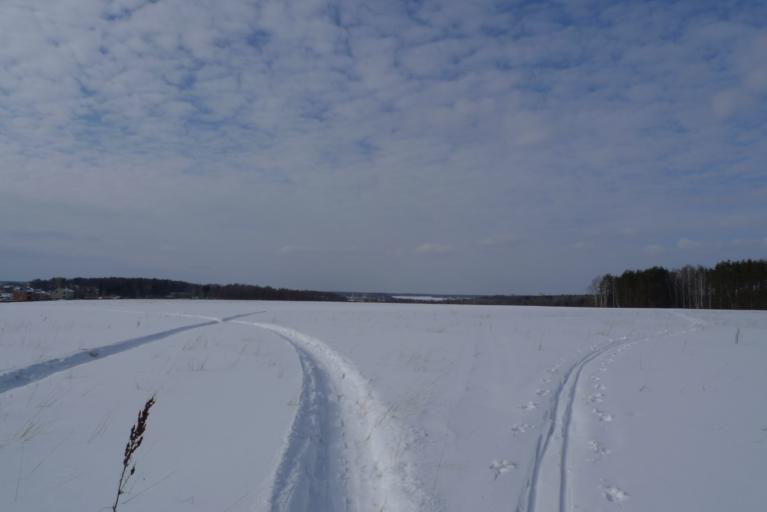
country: RU
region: Moskovskaya
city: Dubrovitsy
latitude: 55.3942
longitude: 37.4913
